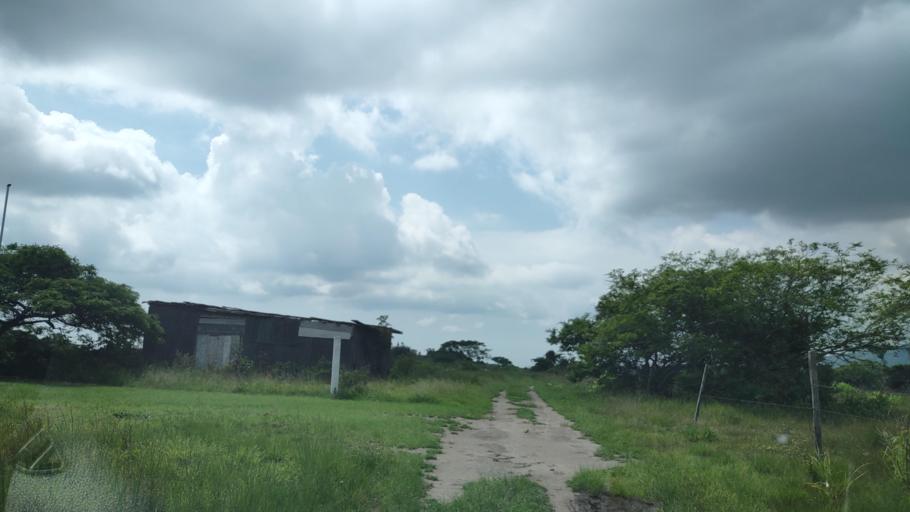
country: MX
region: Veracruz
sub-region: Emiliano Zapata
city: Dos Rios
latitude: 19.4606
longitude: -96.7945
